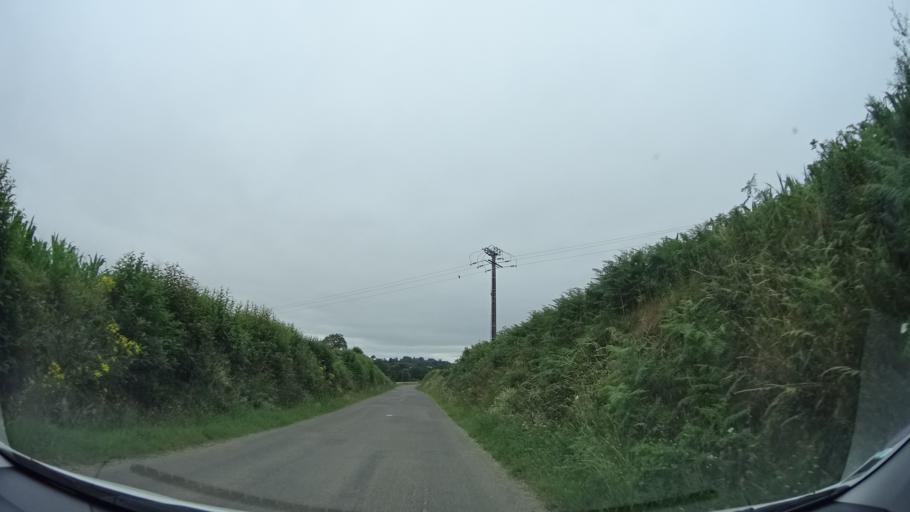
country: FR
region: Brittany
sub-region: Departement d'Ille-et-Vilaine
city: Irodouer
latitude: 48.3144
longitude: -1.9339
